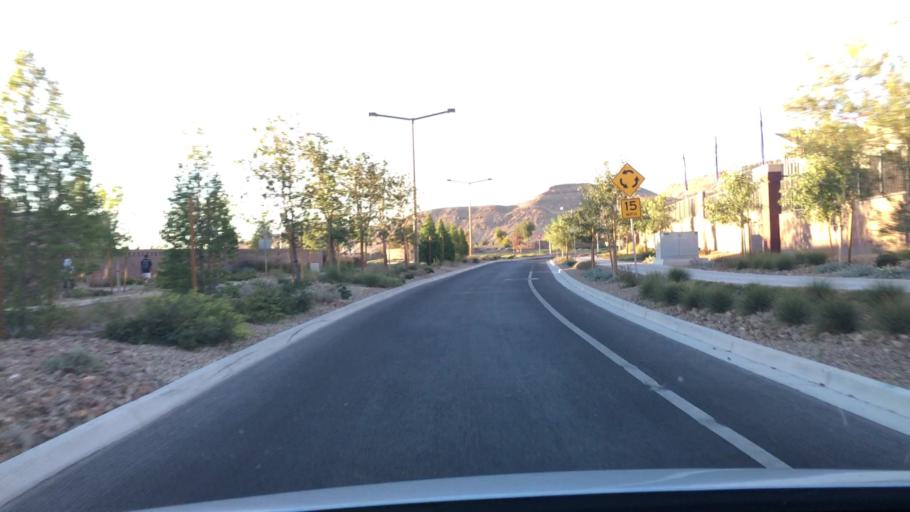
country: US
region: Nevada
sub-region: Clark County
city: Summerlin South
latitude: 36.0763
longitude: -115.3190
